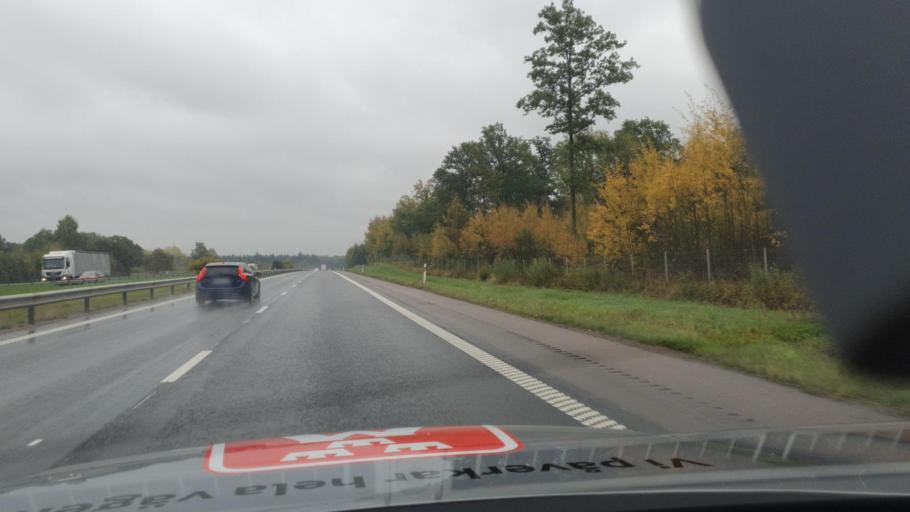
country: SE
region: OEstergoetland
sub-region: Boxholms Kommun
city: Boxholm
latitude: 58.3039
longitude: 14.9652
